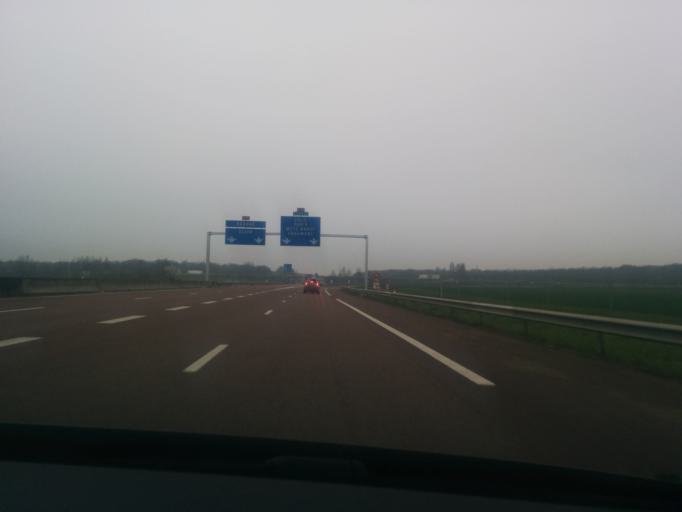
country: FR
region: Bourgogne
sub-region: Departement de la Cote-d'Or
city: Chevigny-Saint-Sauveur
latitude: 47.2728
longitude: 5.1515
